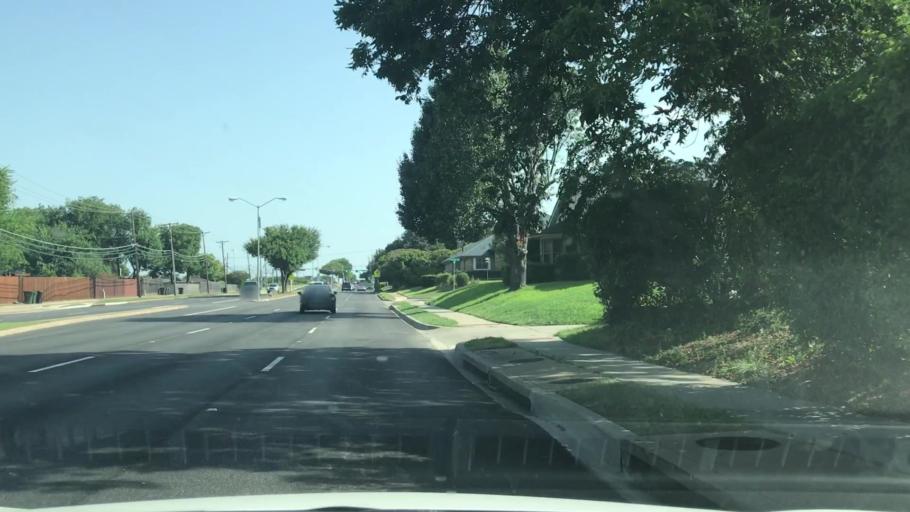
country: US
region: Texas
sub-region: Collin County
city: Plano
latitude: 33.0361
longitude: -96.7535
